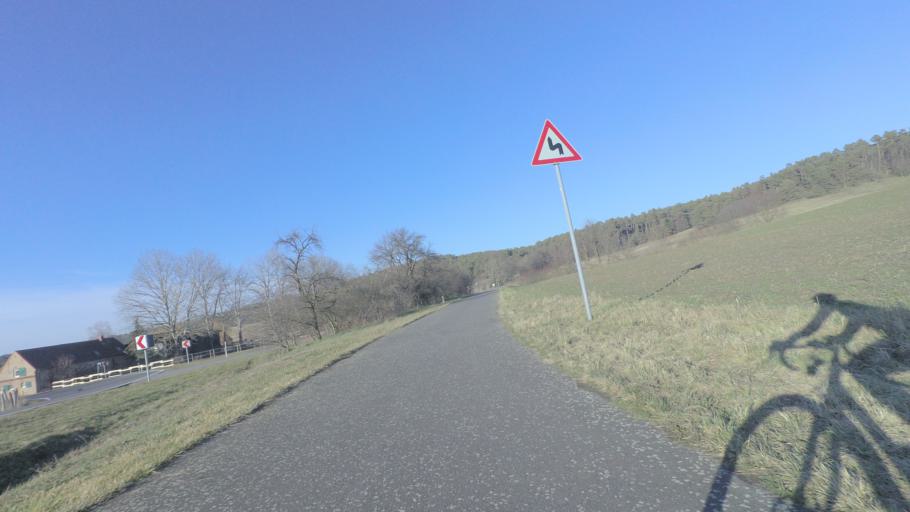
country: DE
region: Brandenburg
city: Ihlow
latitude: 51.9998
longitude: 13.3463
